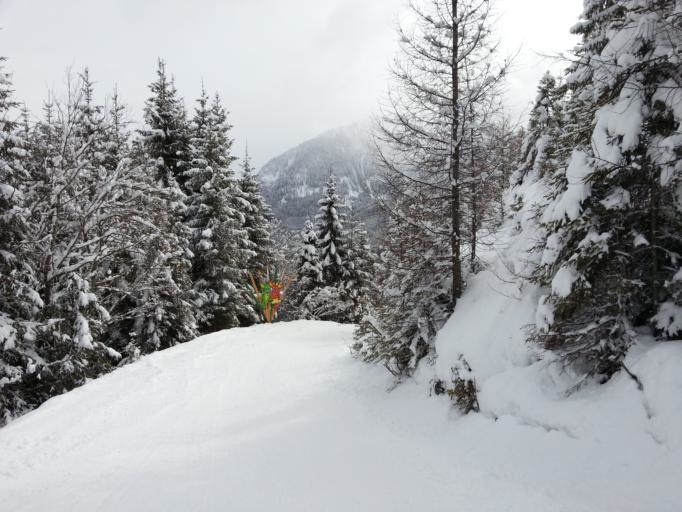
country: AT
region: Salzburg
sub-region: Politischer Bezirk Sankt Johann im Pongau
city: Flachau
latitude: 47.3047
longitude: 13.3820
